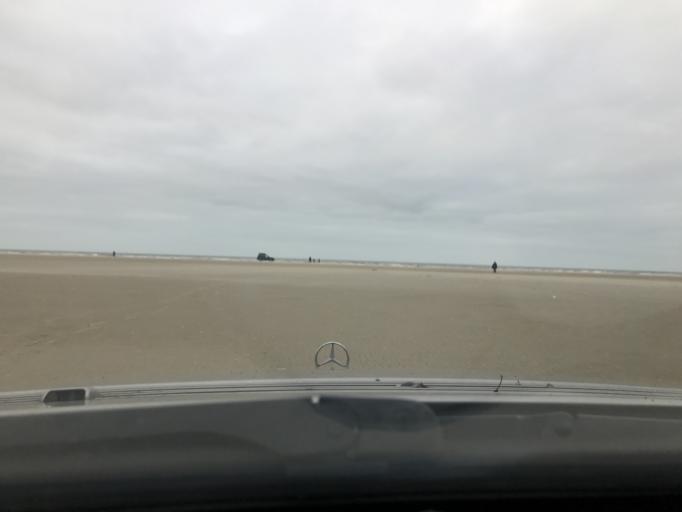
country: DE
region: Schleswig-Holstein
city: List
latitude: 55.1500
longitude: 8.4799
